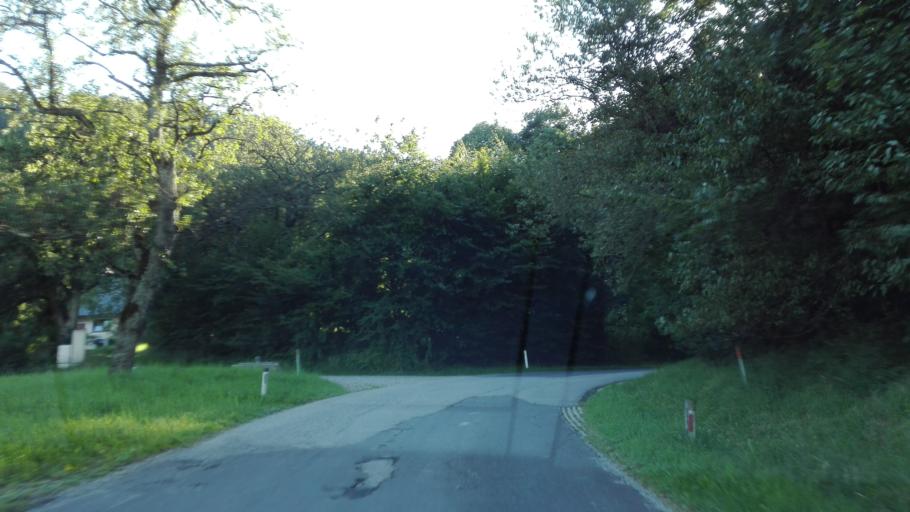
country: AT
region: Lower Austria
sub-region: Politischer Bezirk Sankt Polten
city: Stossing
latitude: 48.0841
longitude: 15.8296
